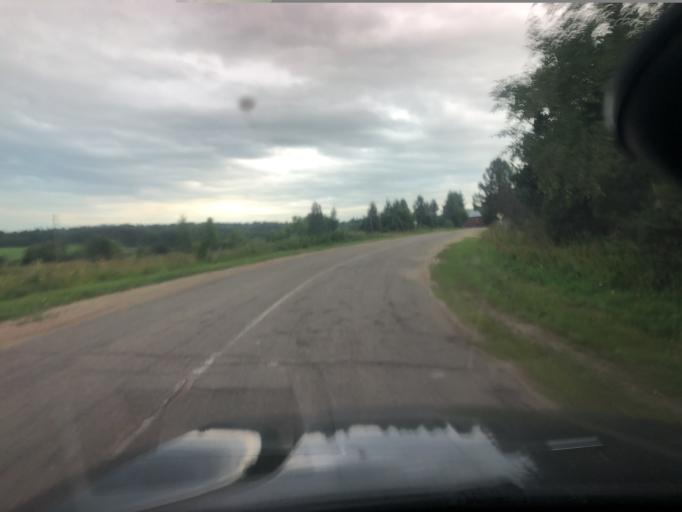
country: RU
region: Jaroslavl
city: Pereslavl'-Zalesskiy
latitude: 57.0314
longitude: 38.9133
